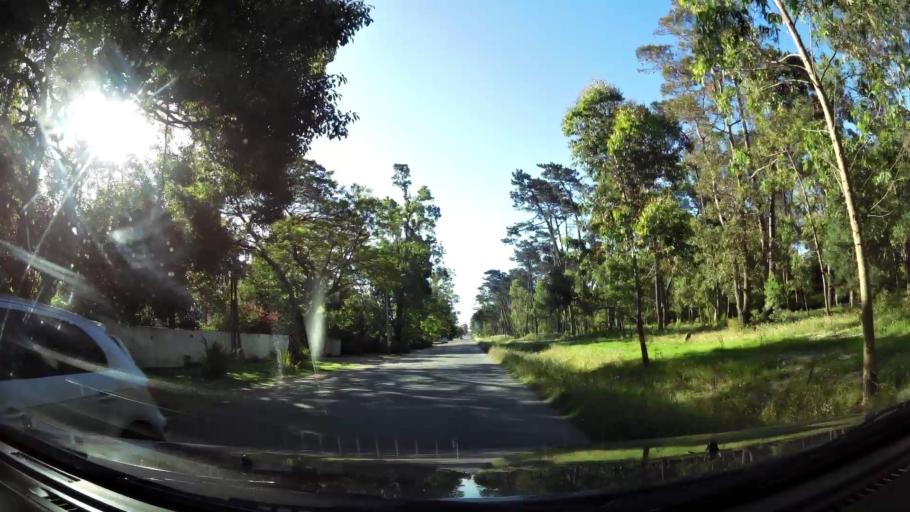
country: UY
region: Canelones
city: Paso de Carrasco
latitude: -34.8564
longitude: -56.0340
